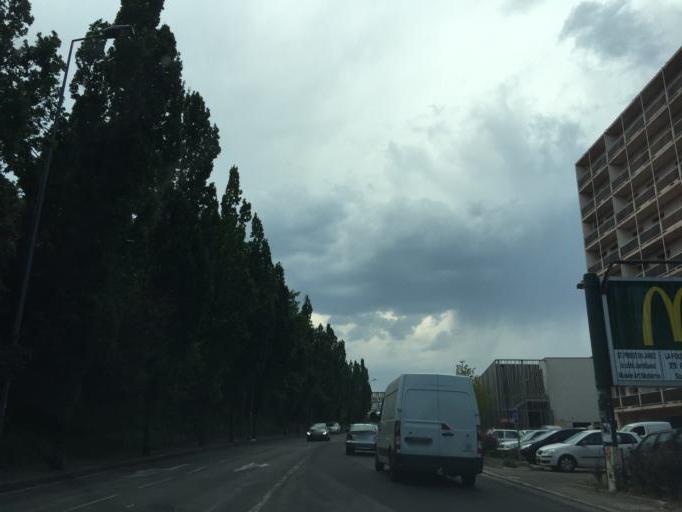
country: FR
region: Rhone-Alpes
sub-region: Departement de la Loire
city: Saint-Etienne
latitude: 45.4491
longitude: 4.3910
